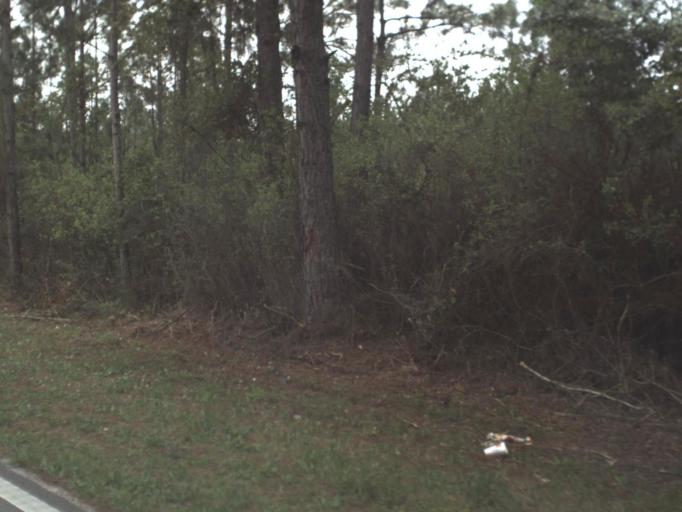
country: US
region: Florida
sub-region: Escambia County
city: Myrtle Grove
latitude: 30.3630
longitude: -87.3526
